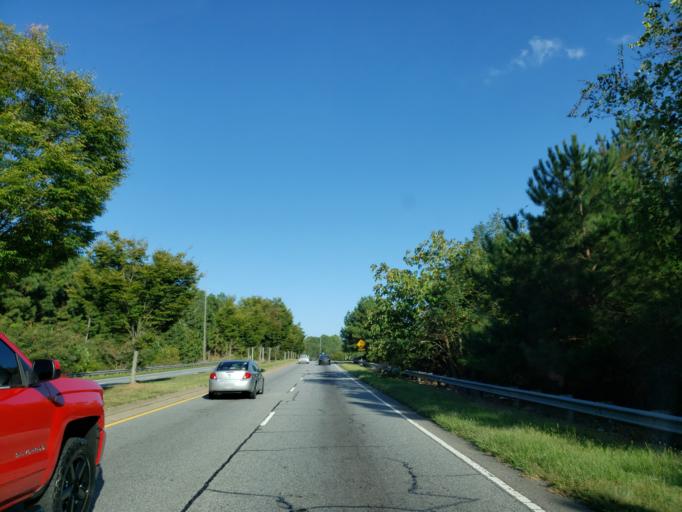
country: US
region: Georgia
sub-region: Cobb County
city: Smyrna
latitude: 33.8427
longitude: -84.5261
